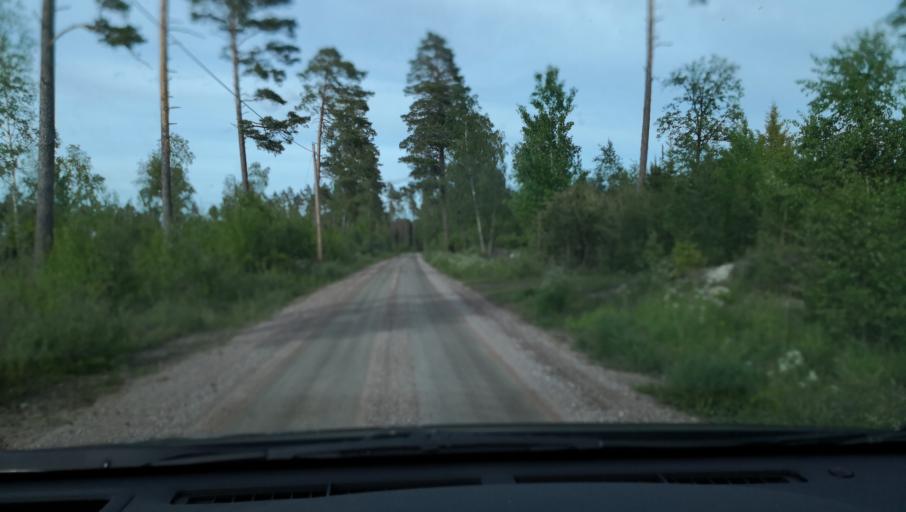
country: SE
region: Vaestmanland
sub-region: Kungsors Kommun
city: Kungsoer
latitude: 59.3717
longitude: 16.0931
